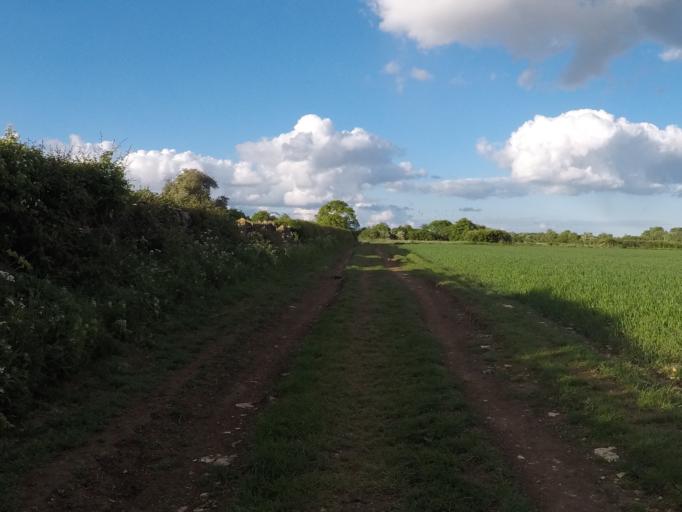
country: GB
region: England
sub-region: Oxfordshire
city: Stonesfield
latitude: 51.8586
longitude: -1.4563
